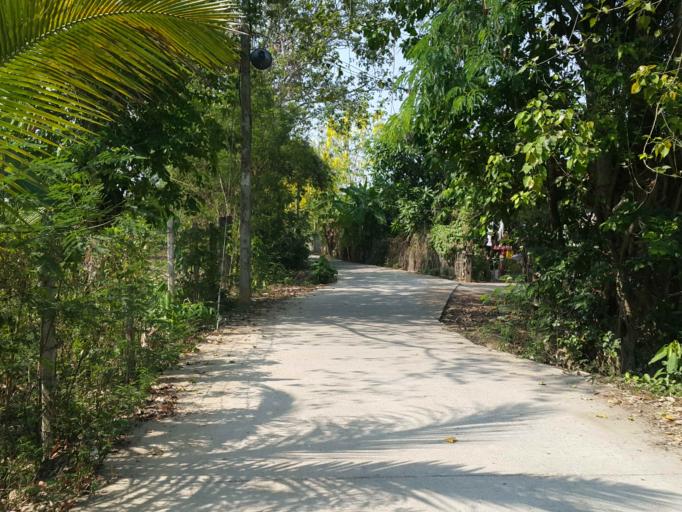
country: TH
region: Chiang Mai
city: San Kamphaeng
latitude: 18.7626
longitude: 99.0717
